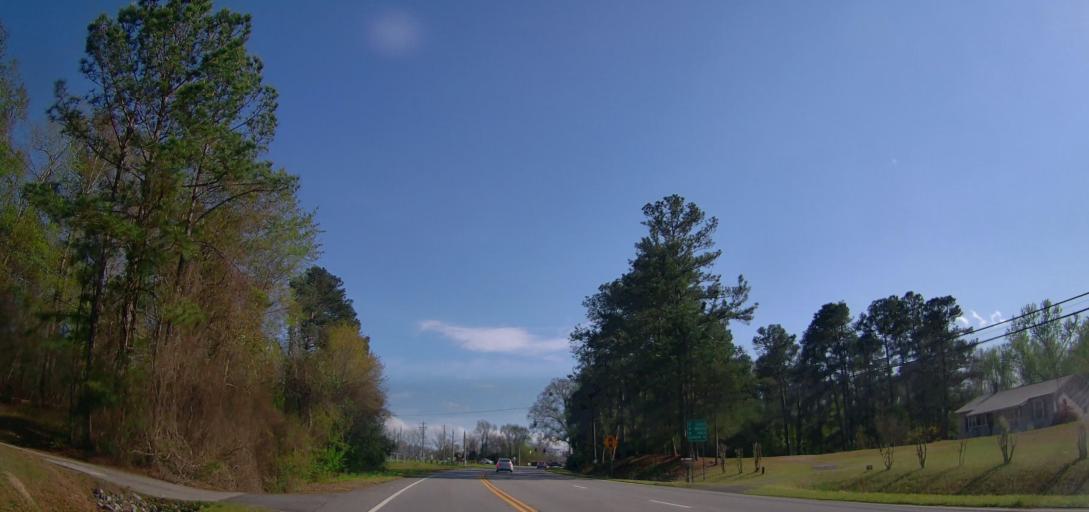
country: US
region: Georgia
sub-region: Baldwin County
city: Hardwick
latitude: 33.0256
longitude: -83.2347
